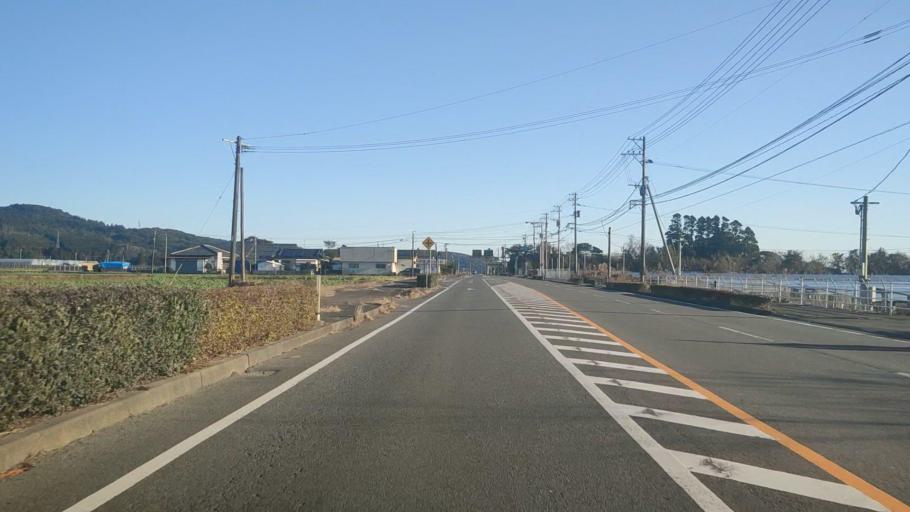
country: JP
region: Miyazaki
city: Takanabe
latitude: 32.3210
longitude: 131.5950
